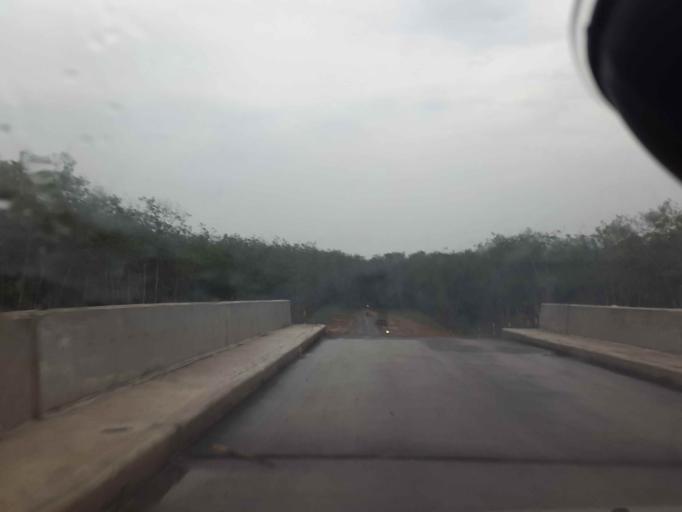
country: ID
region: Lampung
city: Kedaton
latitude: -5.3778
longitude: 105.3302
